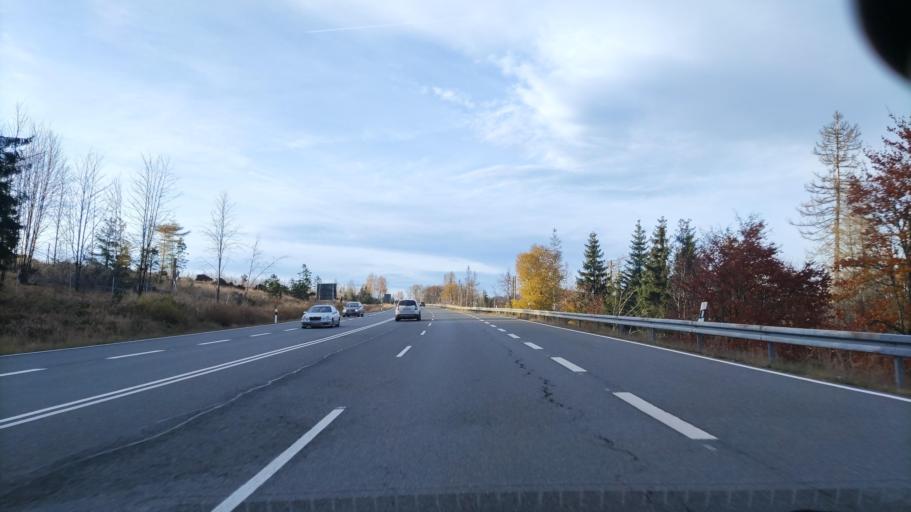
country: DE
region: Lower Saxony
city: Braunlage
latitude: 51.7420
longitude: 10.5867
